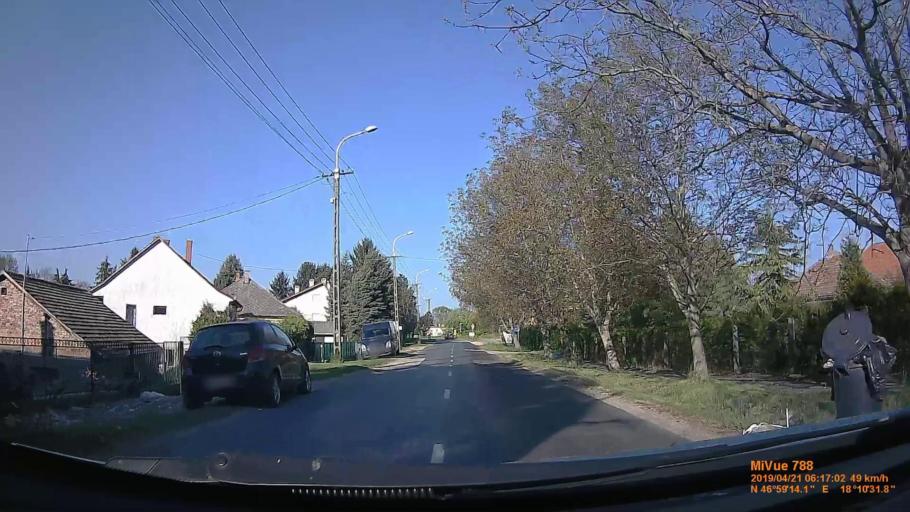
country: HU
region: Fejer
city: Lepseny
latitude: 46.9873
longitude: 18.1755
